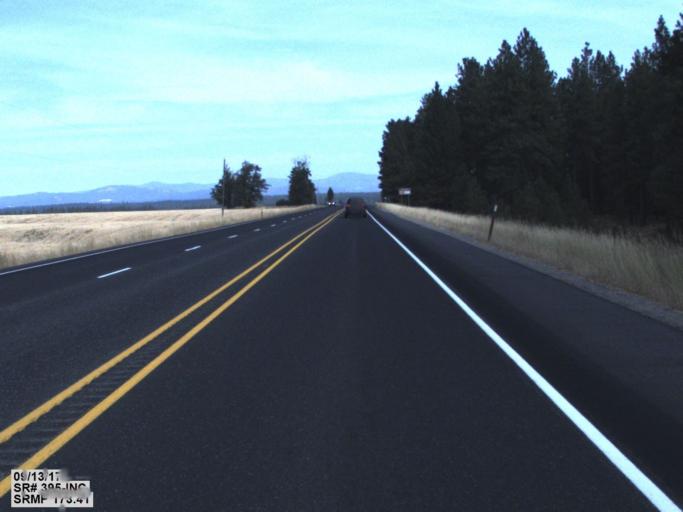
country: US
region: Washington
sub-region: Spokane County
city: Fairwood
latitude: 47.8648
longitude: -117.4220
